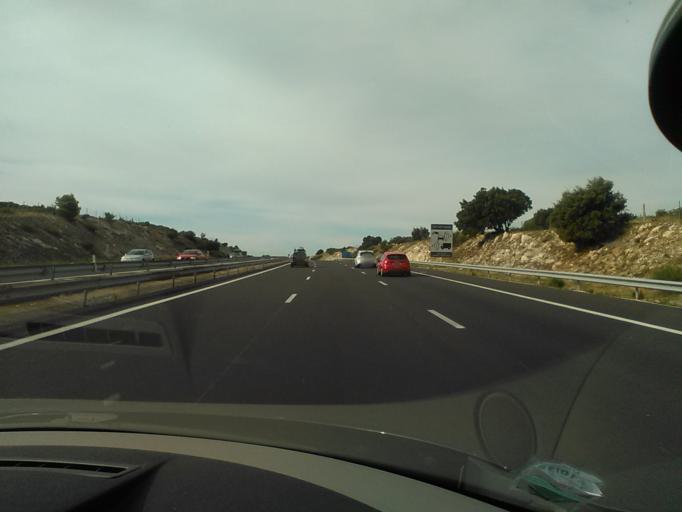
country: FR
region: Languedoc-Roussillon
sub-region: Departement du Gard
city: Remoulins
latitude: 43.9527
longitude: 4.6228
